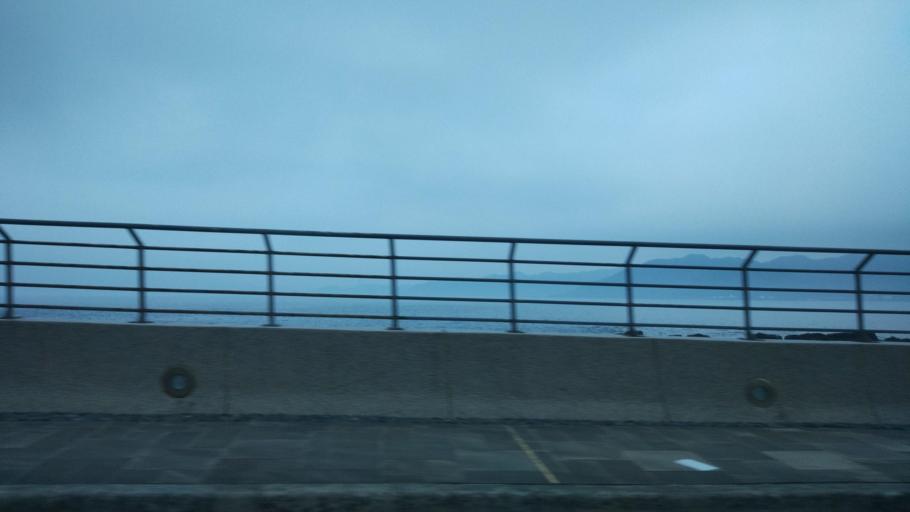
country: TW
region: Taiwan
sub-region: Keelung
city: Keelung
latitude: 25.2011
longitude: 121.6933
